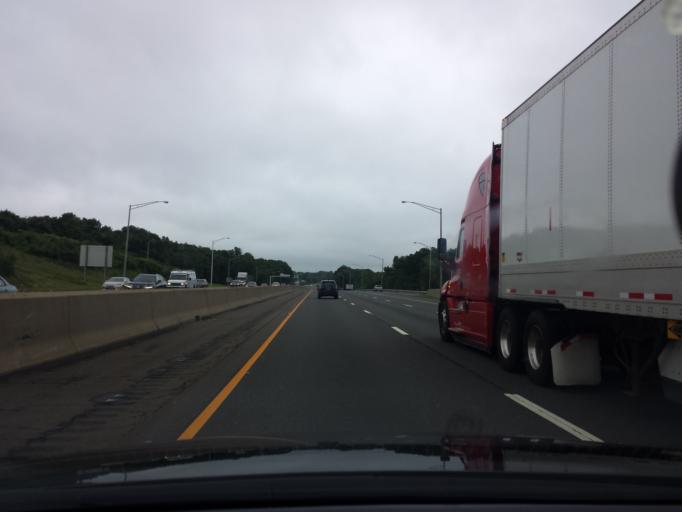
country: US
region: Connecticut
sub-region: New Haven County
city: Woodmont
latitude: 41.2540
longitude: -72.9985
